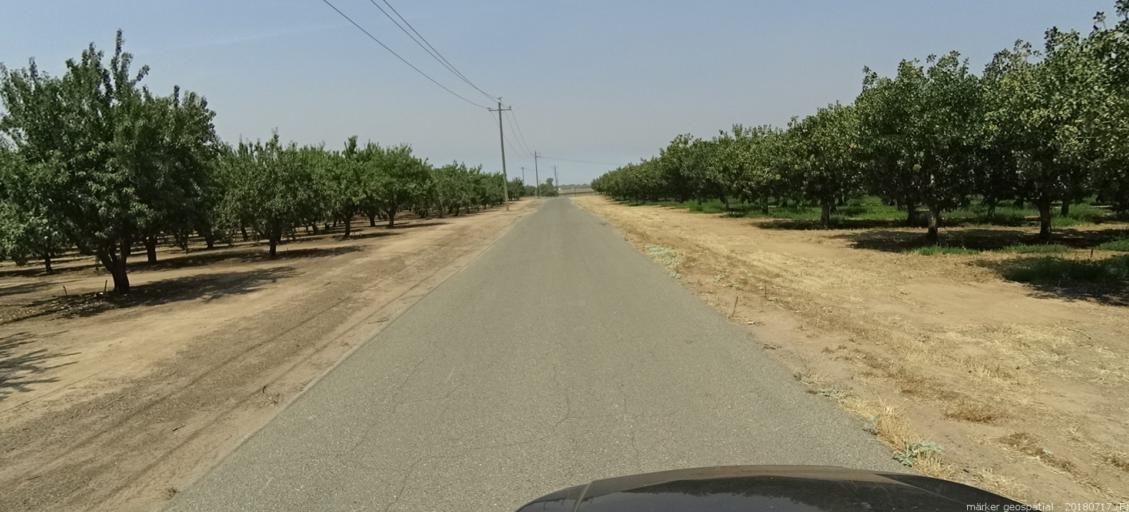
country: US
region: California
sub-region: Madera County
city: Fairmead
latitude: 37.1343
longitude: -120.1543
